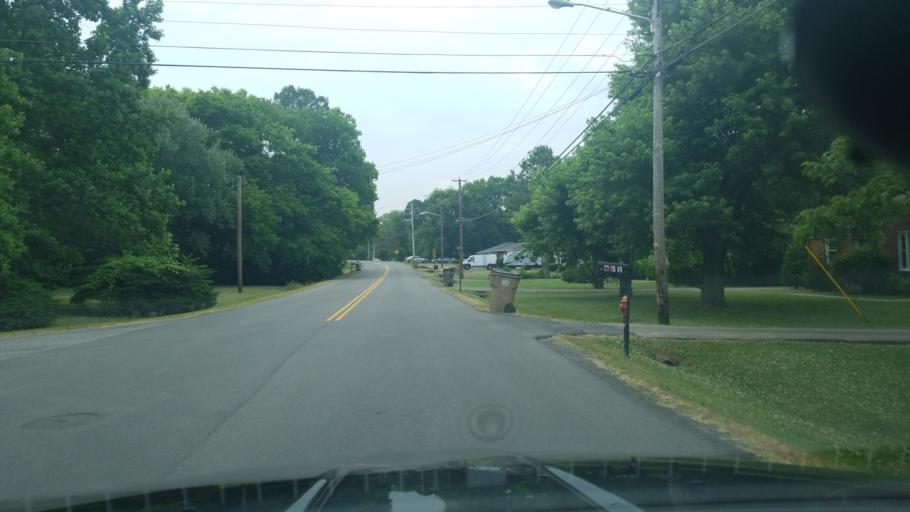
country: US
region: Tennessee
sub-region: Davidson County
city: Goodlettsville
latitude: 36.2646
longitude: -86.7453
